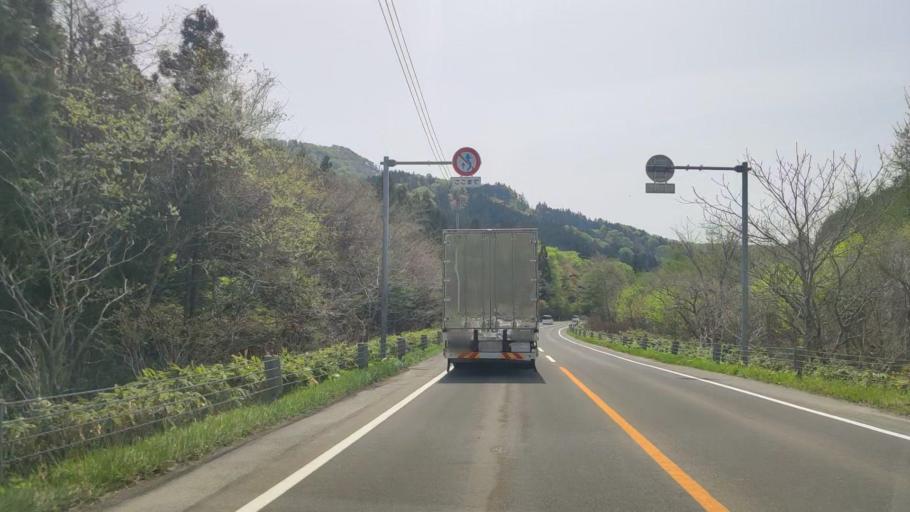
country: JP
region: Aomori
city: Aomori Shi
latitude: 40.7806
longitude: 141.0315
